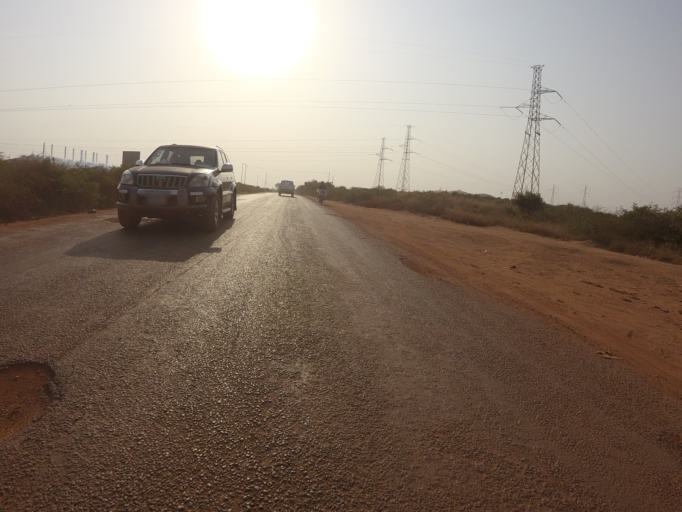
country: GH
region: Greater Accra
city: Tema
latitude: 5.6713
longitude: 0.0205
